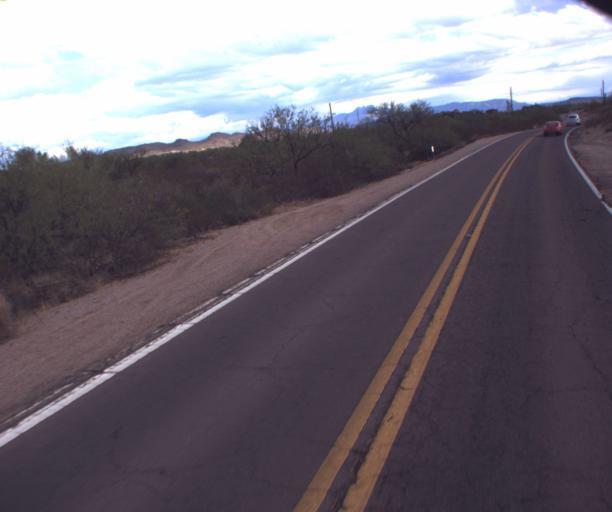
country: US
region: Arizona
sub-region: Pinal County
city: Apache Junction
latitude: 33.4500
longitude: -111.4990
